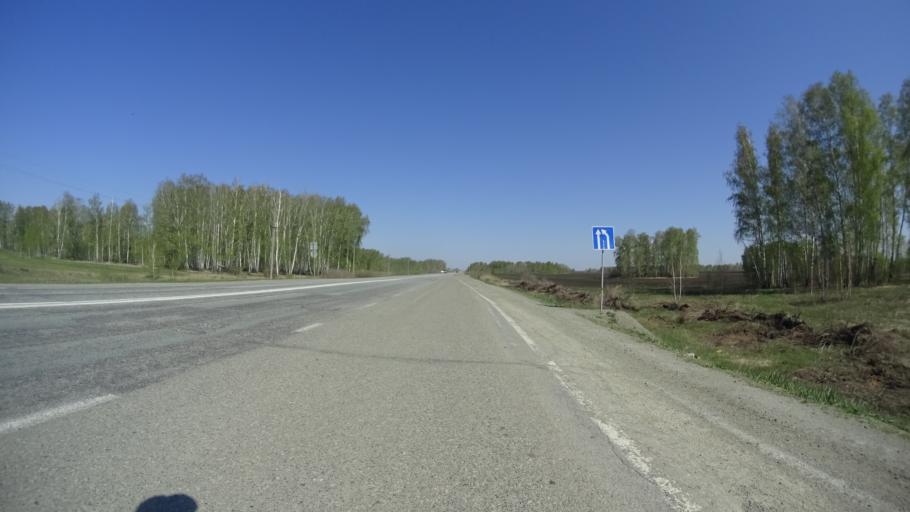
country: RU
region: Chelyabinsk
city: Troitsk
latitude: 54.1775
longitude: 61.4353
